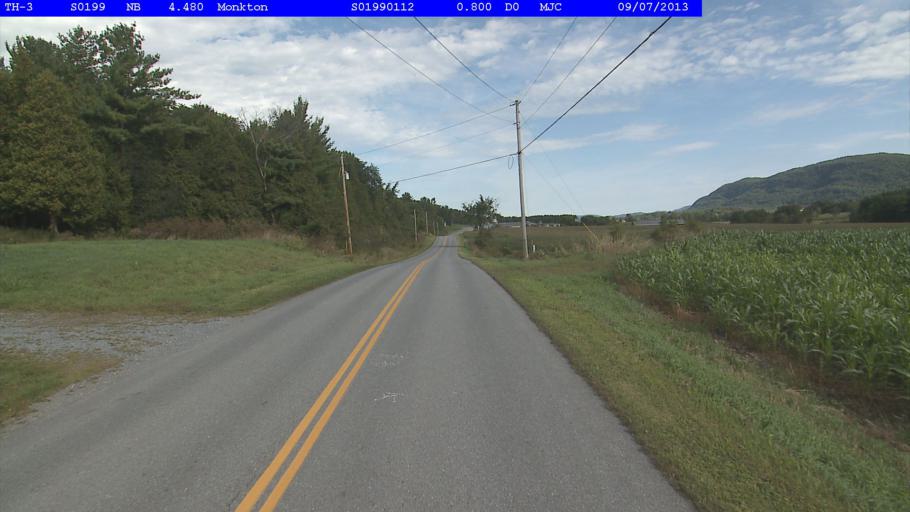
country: US
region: Vermont
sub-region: Addison County
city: Bristol
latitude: 44.1921
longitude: -73.1089
